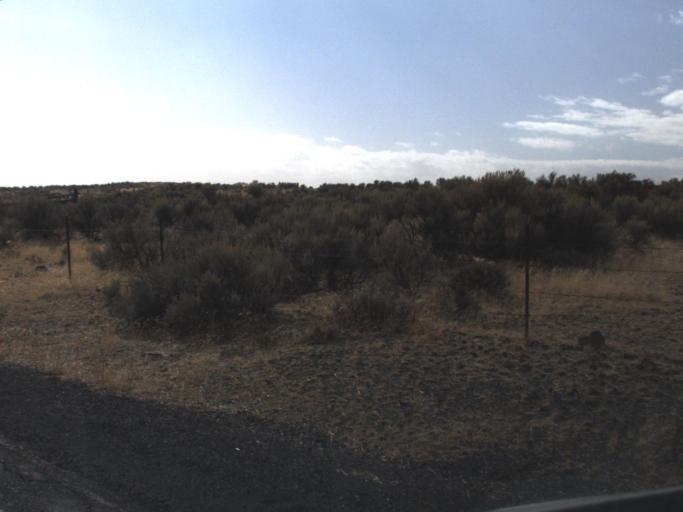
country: US
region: Washington
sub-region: Adams County
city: Ritzville
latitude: 47.4104
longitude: -118.6835
